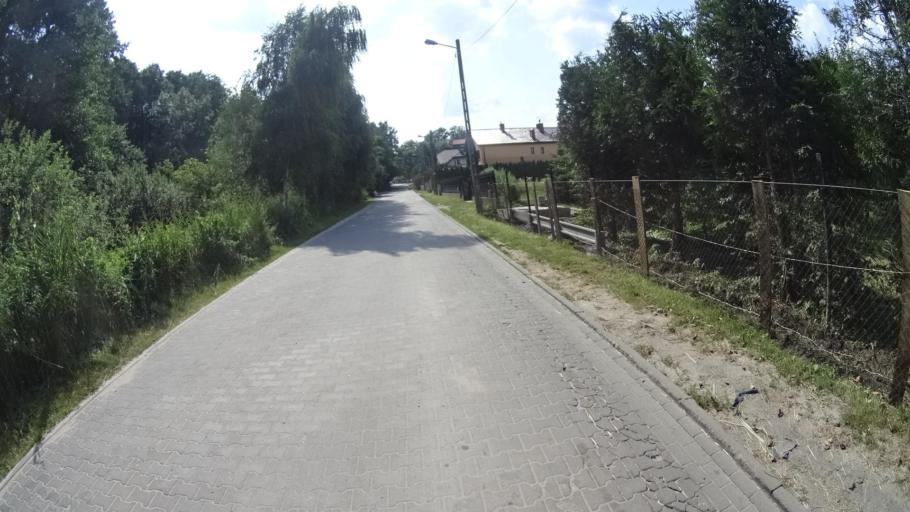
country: PL
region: Masovian Voivodeship
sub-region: Warszawa
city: Ursynow
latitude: 52.1686
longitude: 21.0491
